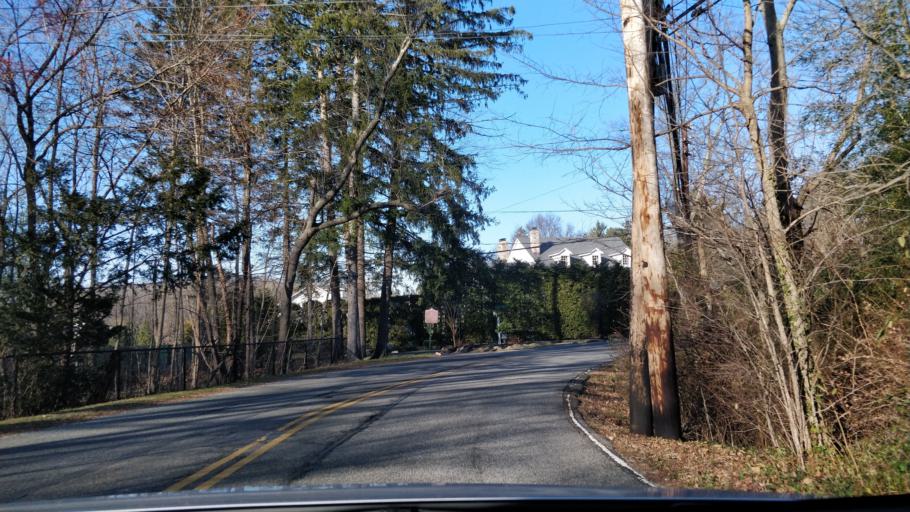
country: US
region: New York
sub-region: Nassau County
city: Glen Head
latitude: 40.8264
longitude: -73.6163
